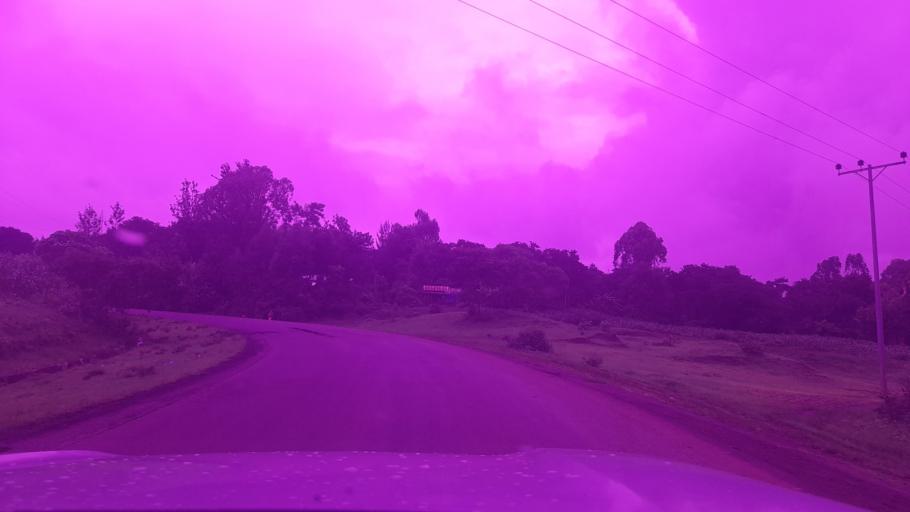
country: ET
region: Oromiya
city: Jima
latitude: 7.7492
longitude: 37.1631
